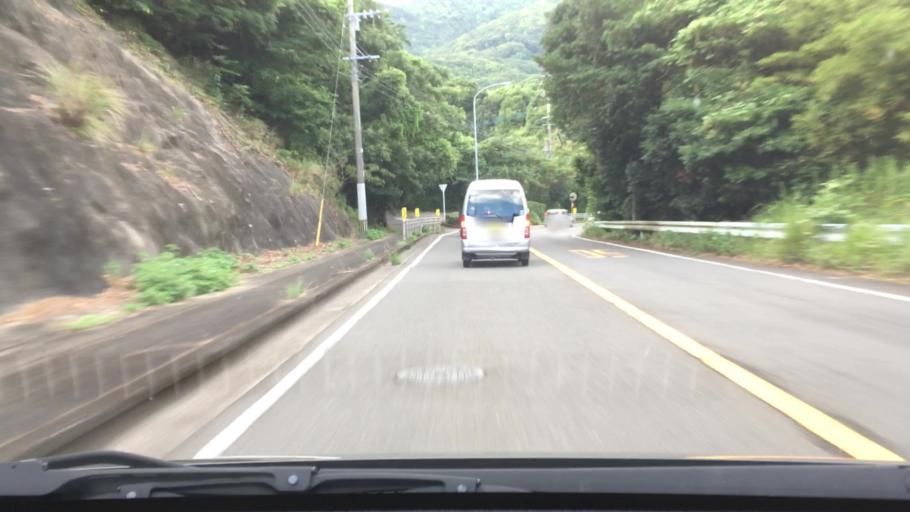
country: JP
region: Nagasaki
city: Togitsu
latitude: 32.8227
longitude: 129.7329
